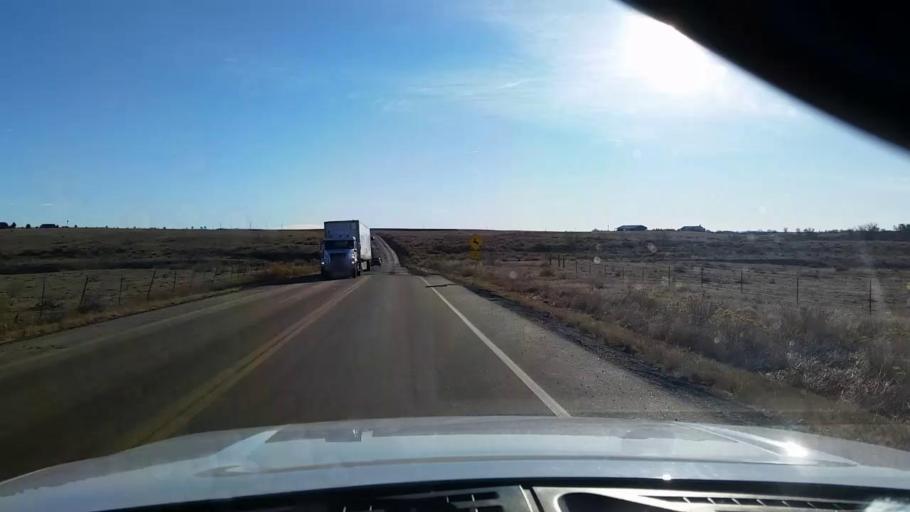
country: US
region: Colorado
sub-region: Larimer County
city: Wellington
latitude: 40.7709
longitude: -105.1198
